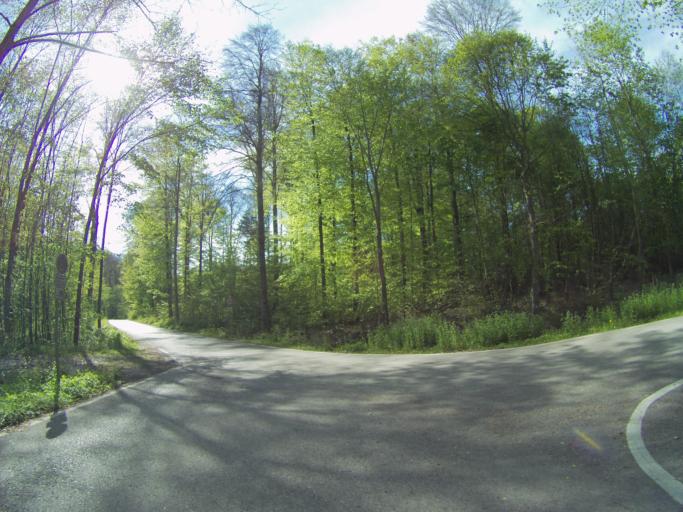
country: DE
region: Bavaria
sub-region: Upper Bavaria
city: Freising
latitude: 48.4169
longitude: 11.7354
